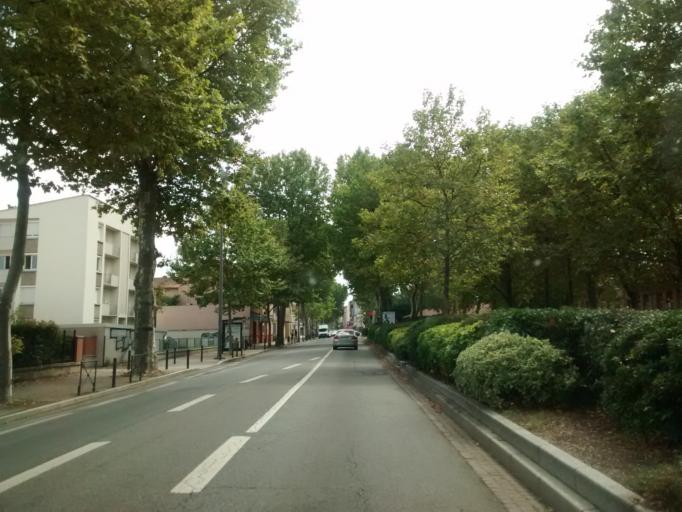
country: FR
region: Midi-Pyrenees
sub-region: Departement de la Haute-Garonne
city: L'Union
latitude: 43.6371
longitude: 1.4646
